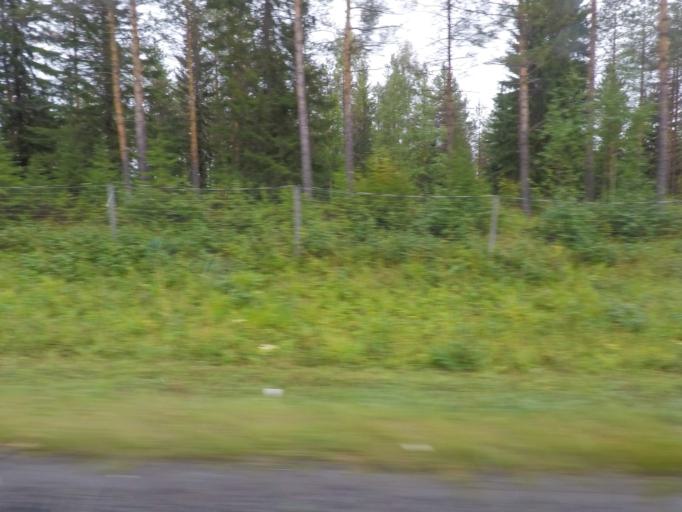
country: FI
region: Southern Savonia
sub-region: Pieksaemaeki
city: Juva
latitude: 61.9856
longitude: 27.8032
